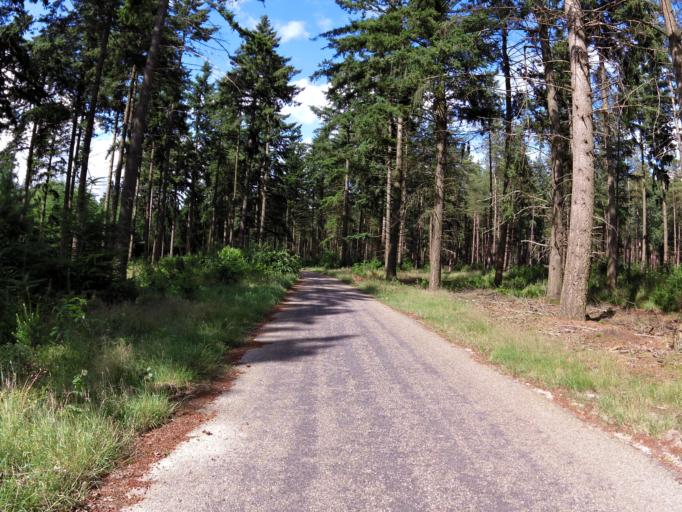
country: NL
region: North Brabant
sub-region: Gemeente Valkenswaard
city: Valkenswaard
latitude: 51.3447
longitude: 5.5131
